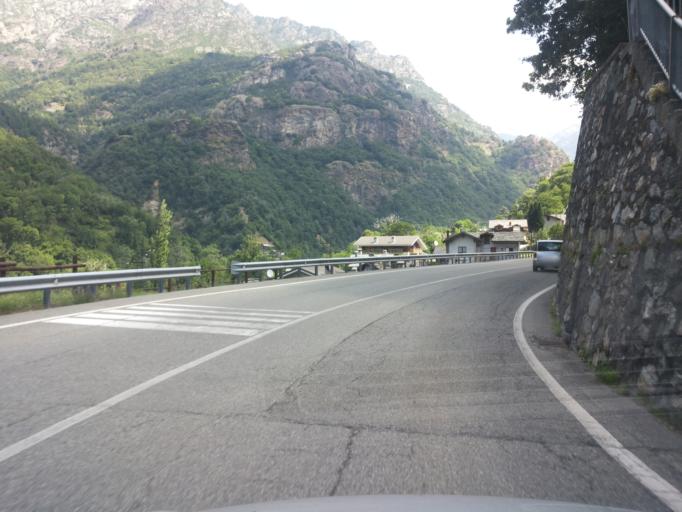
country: IT
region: Aosta Valley
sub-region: Valle d'Aosta
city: Perloz
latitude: 45.6159
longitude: 7.8158
